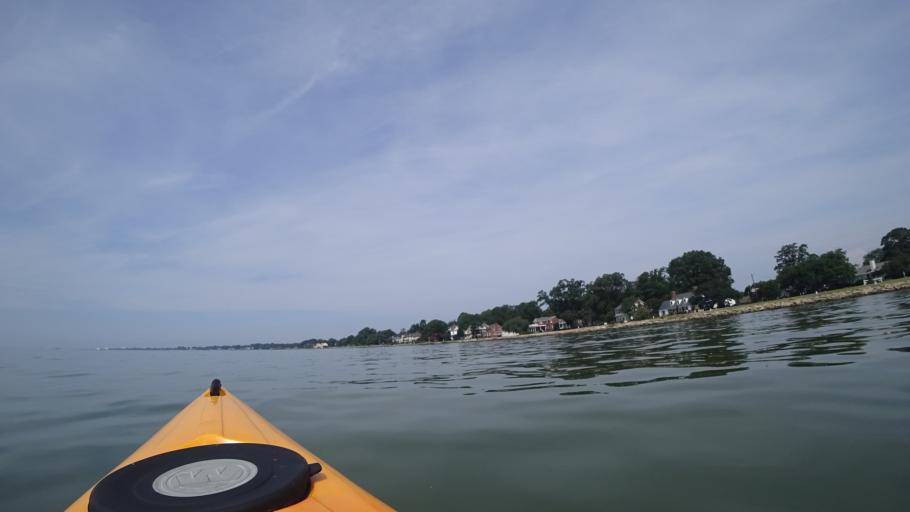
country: US
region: Virginia
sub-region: City of Hampton
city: Hampton
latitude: 37.0009
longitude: -76.3634
